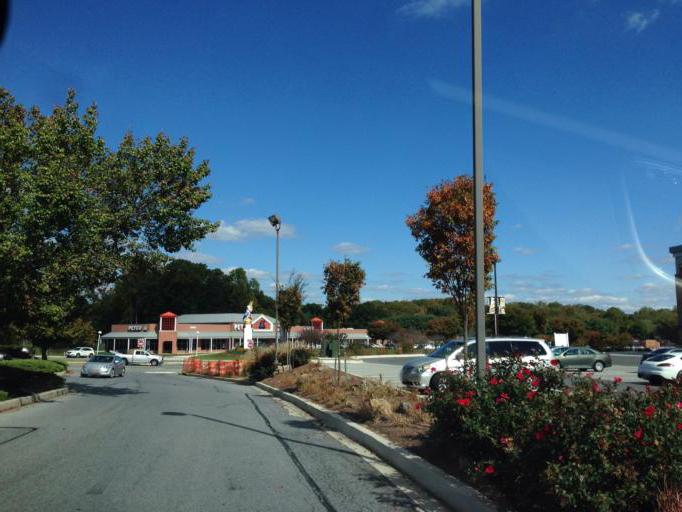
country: US
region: Maryland
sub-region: Howard County
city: Columbia
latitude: 39.2784
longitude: -76.8582
